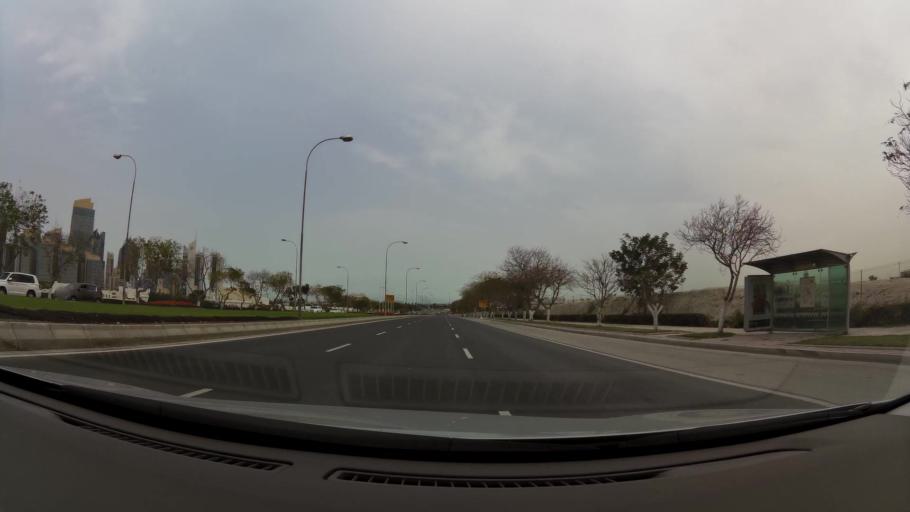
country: QA
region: Baladiyat ad Dawhah
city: Doha
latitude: 25.3123
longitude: 51.5086
